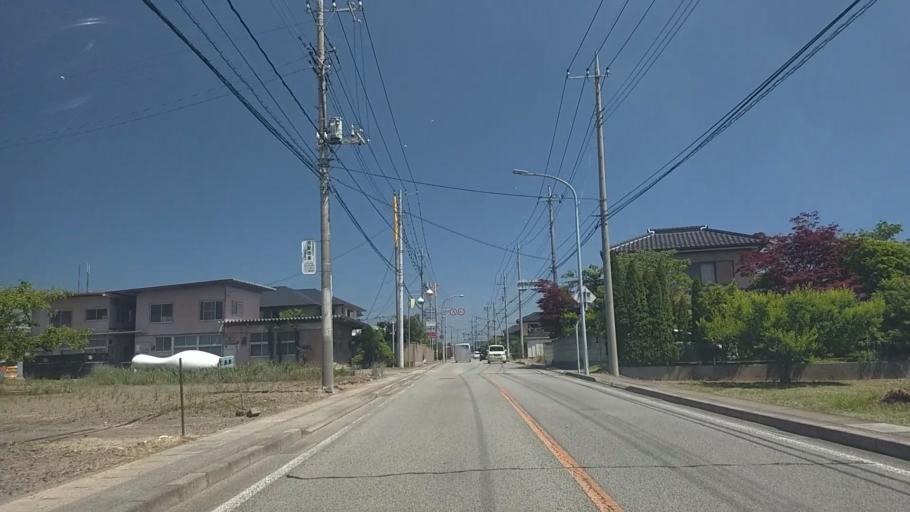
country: JP
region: Yamanashi
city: Ryuo
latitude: 35.6456
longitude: 138.4636
